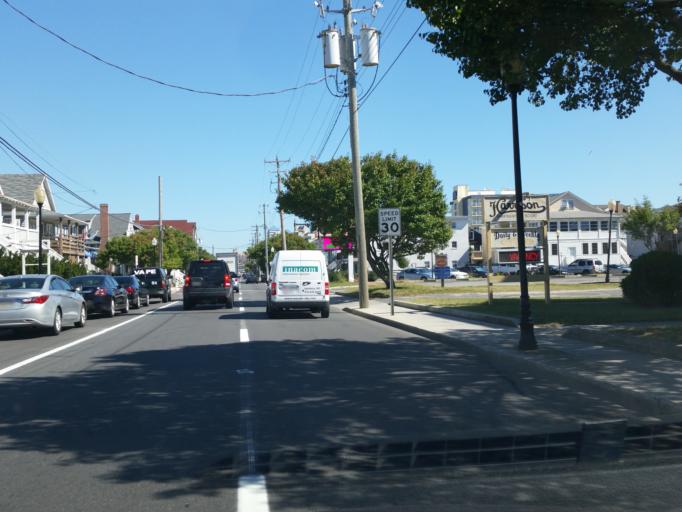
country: US
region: Maryland
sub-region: Worcester County
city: Ocean City
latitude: 38.3402
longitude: -75.0816
